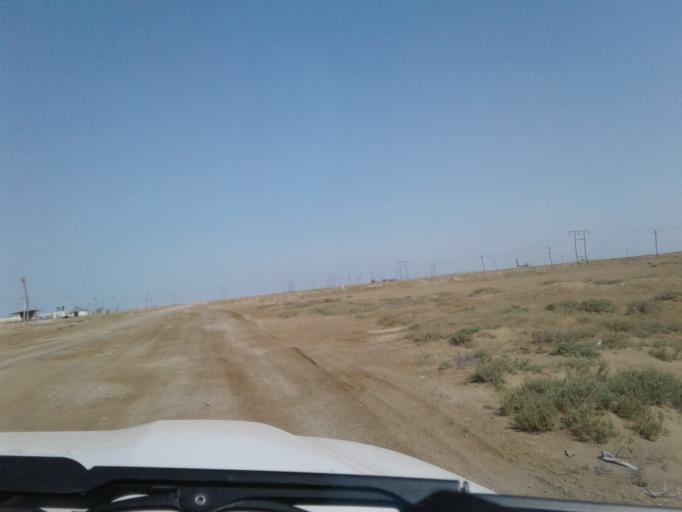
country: IR
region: Golestan
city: Gomishan
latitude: 37.7671
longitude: 53.9216
